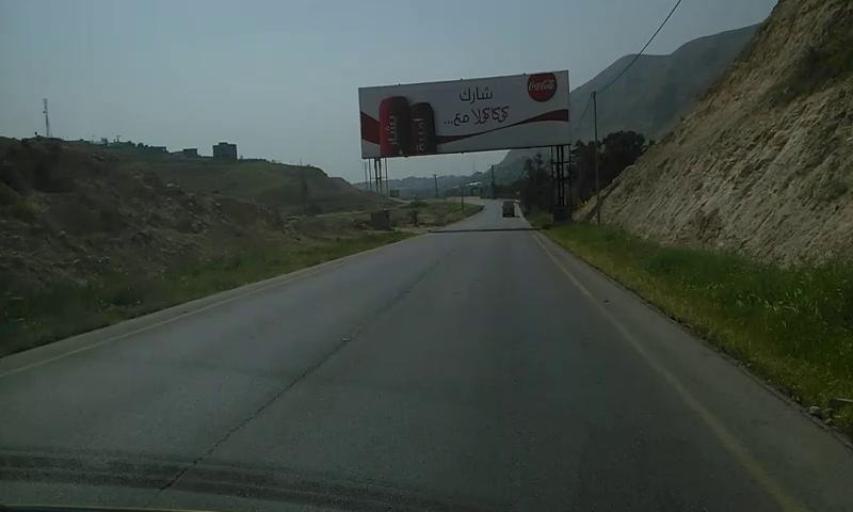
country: PS
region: West Bank
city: An Nuway`imah
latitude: 31.8943
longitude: 35.4290
